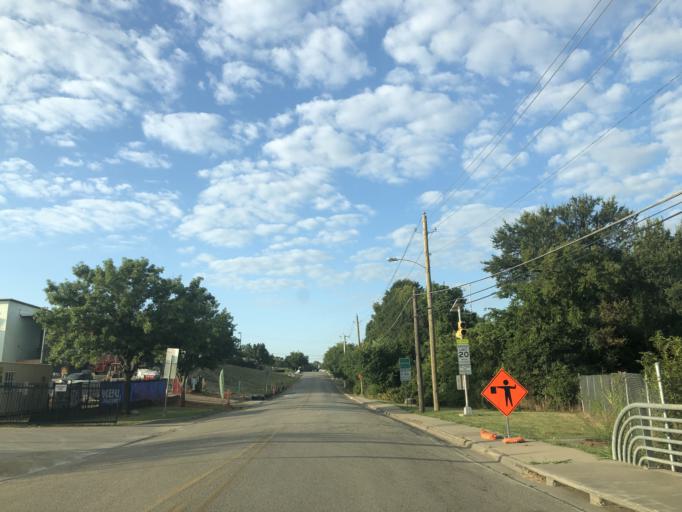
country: US
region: Texas
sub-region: Dallas County
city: Grand Prairie
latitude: 32.7584
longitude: -97.0123
